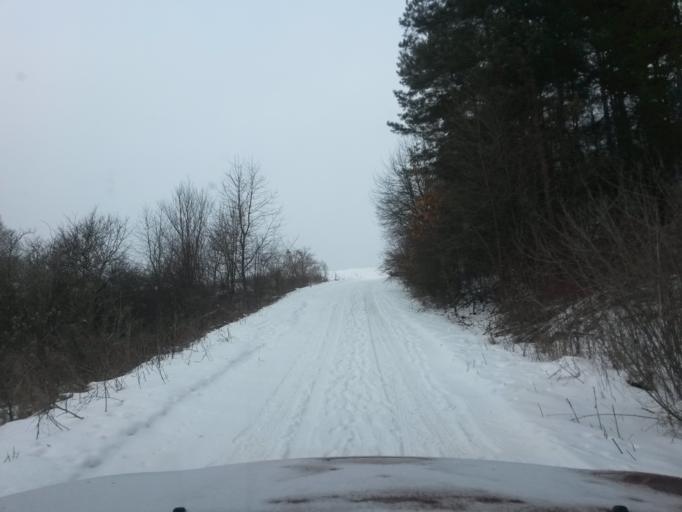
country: SK
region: Presovsky
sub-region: Okres Presov
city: Presov
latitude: 48.9195
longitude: 21.1824
